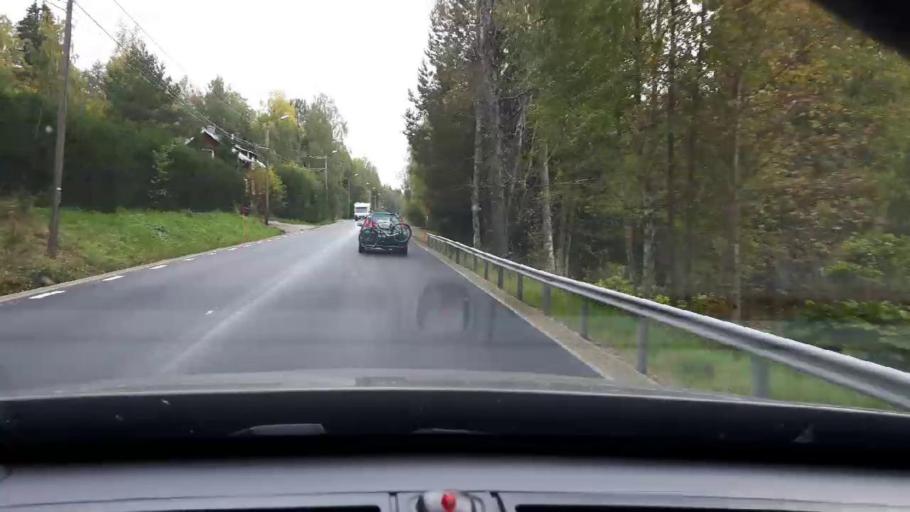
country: SE
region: Dalarna
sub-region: Ludvika Kommun
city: Ludvika
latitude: 60.1981
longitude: 15.1348
